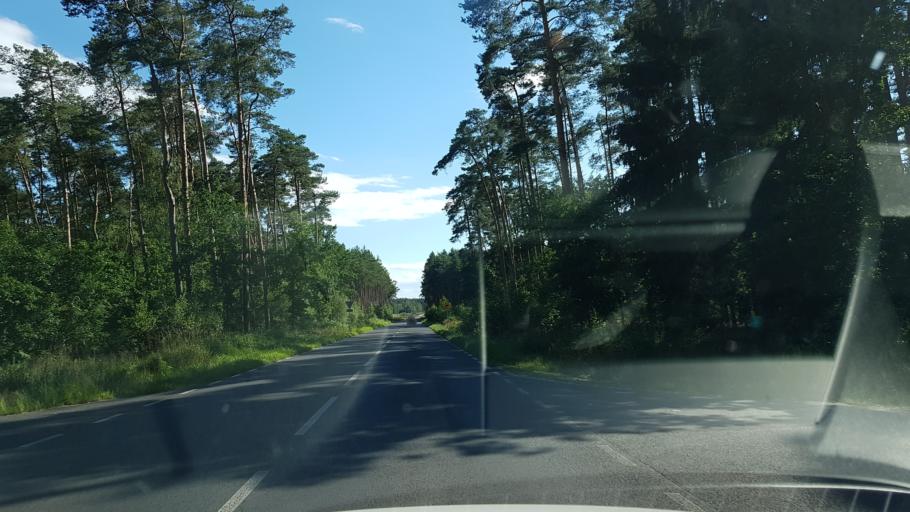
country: PL
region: West Pomeranian Voivodeship
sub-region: Powiat goleniowski
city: Goleniow
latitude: 53.5722
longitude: 14.7892
